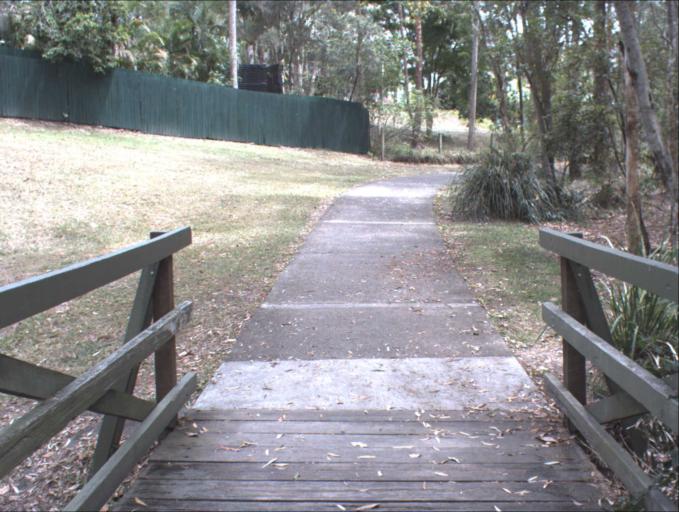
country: AU
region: Queensland
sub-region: Logan
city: Slacks Creek
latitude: -27.6541
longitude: 153.1917
